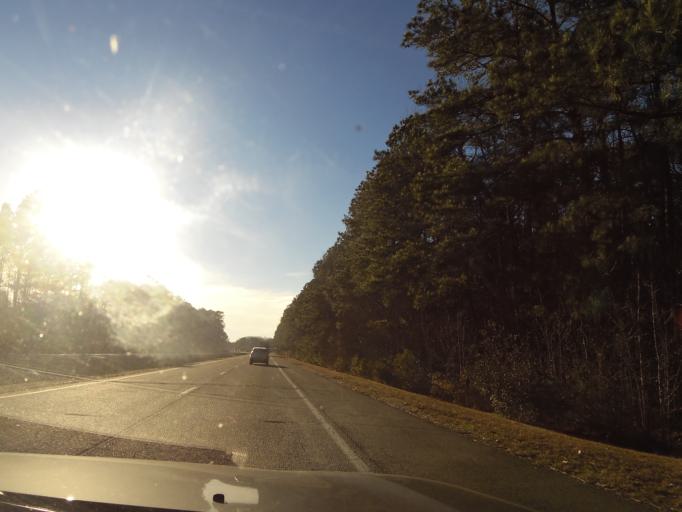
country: US
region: Virginia
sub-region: Isle of Wight County
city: Windsor
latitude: 36.6767
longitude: -76.7782
